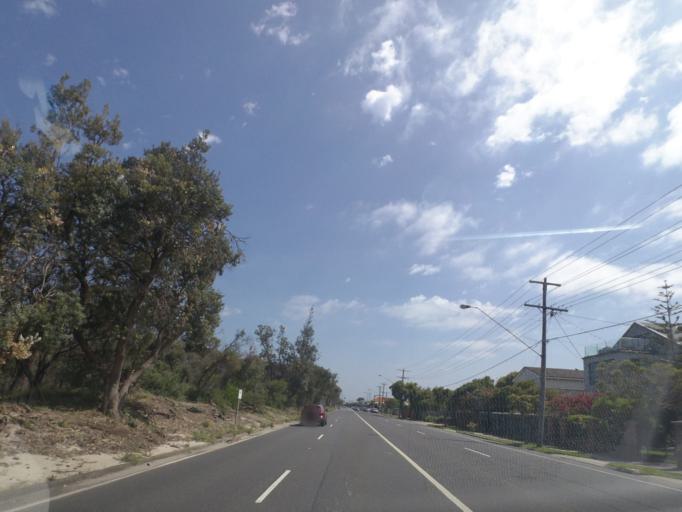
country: AU
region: Victoria
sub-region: Frankston
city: Seaford
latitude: -38.1059
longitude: 145.1258
